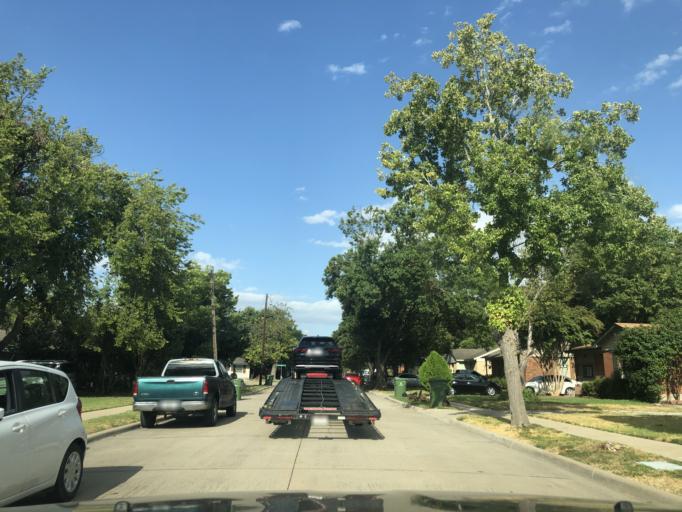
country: US
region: Texas
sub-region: Dallas County
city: Garland
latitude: 32.8885
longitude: -96.6554
